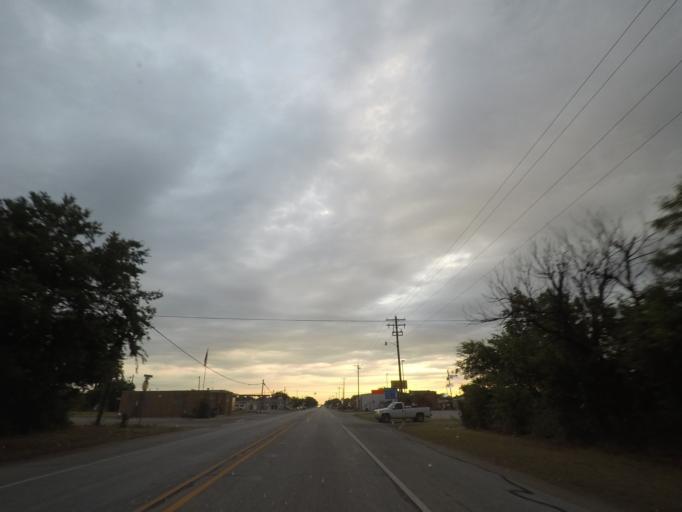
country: US
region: Texas
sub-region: Clay County
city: Henrietta
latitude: 34.0123
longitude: -98.2339
